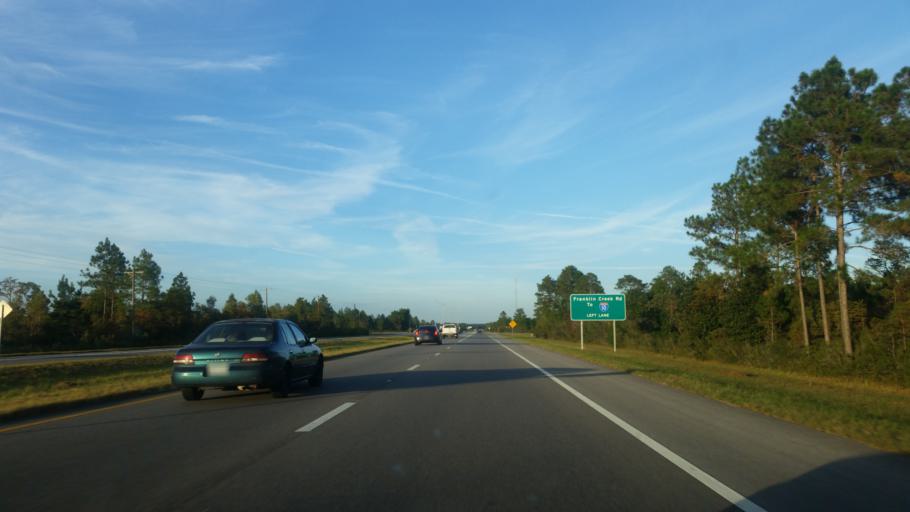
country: US
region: Alabama
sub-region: Mobile County
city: Grand Bay
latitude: 30.4550
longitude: -88.4199
